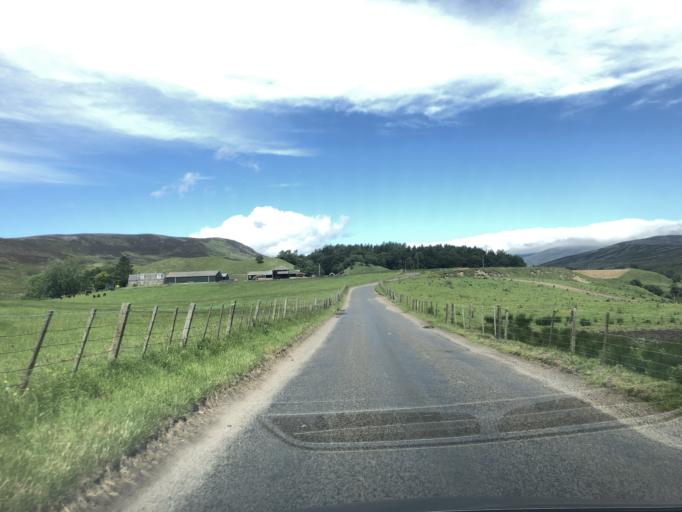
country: GB
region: Scotland
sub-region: Angus
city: Kirriemuir
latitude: 56.7584
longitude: -3.0177
